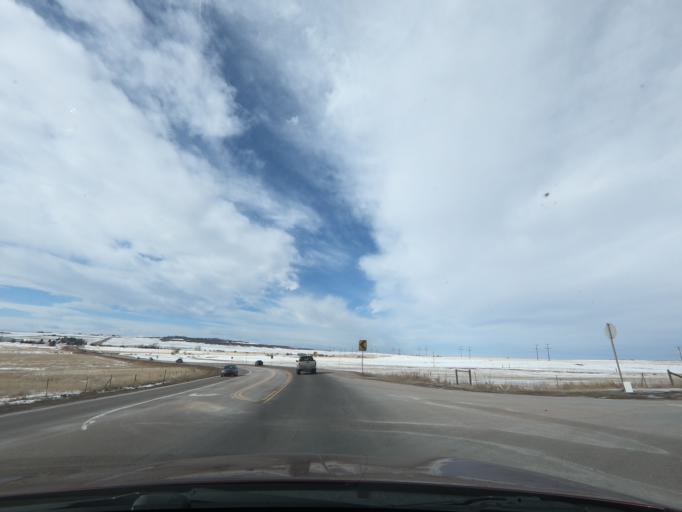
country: US
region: Colorado
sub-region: Elbert County
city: Elizabeth
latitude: 39.2610
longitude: -104.7035
